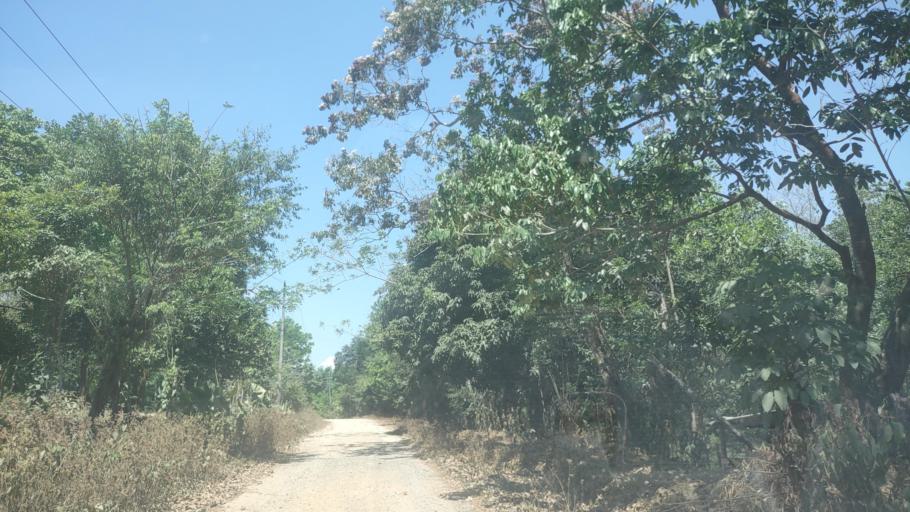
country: MX
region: Veracruz
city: Las Choapas
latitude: 17.7871
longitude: -94.1599
